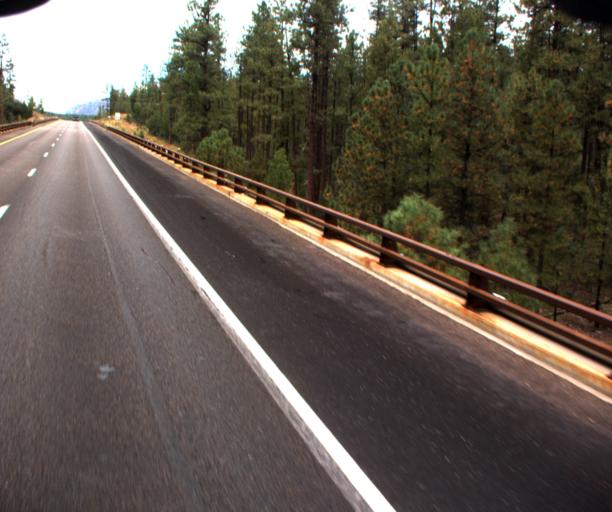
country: US
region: Arizona
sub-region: Gila County
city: Star Valley
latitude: 34.3099
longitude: -111.1097
